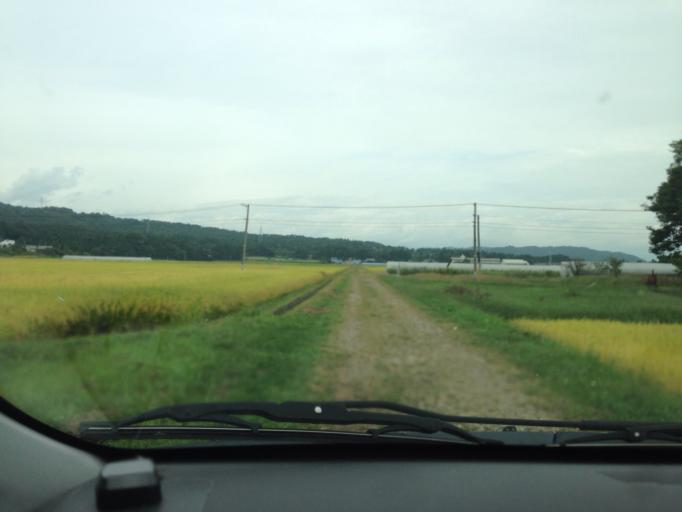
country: JP
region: Fukushima
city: Kitakata
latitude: 37.5807
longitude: 139.8082
